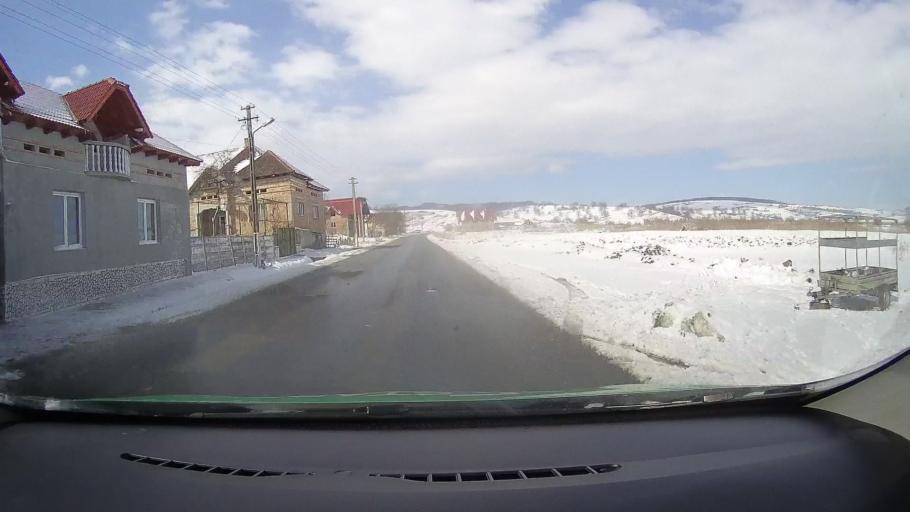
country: RO
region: Sibiu
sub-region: Comuna Altina
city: Altina
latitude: 45.9385
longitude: 24.4577
